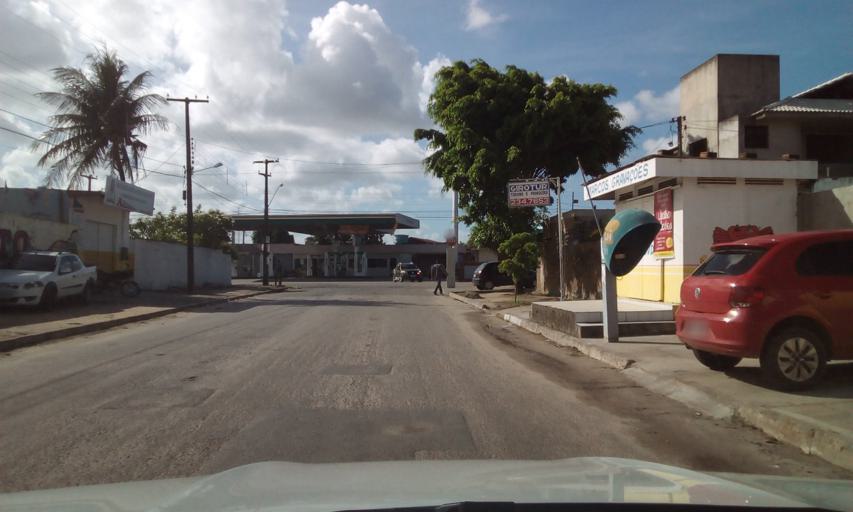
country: BR
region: Paraiba
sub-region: Joao Pessoa
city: Joao Pessoa
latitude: -7.1781
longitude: -34.8798
